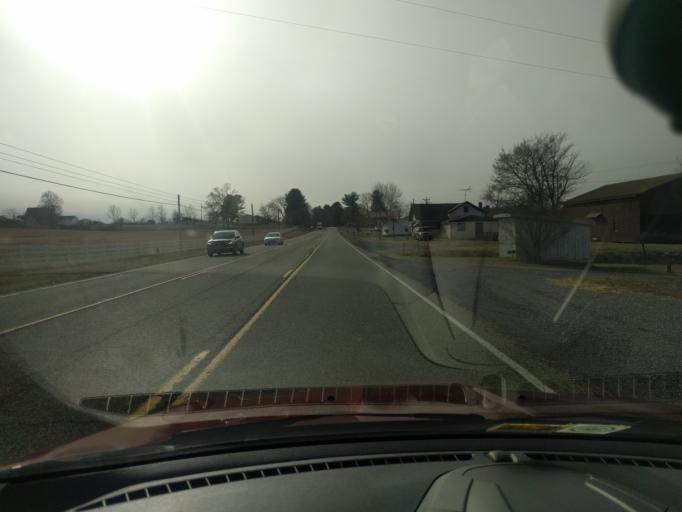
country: US
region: Virginia
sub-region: Augusta County
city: Stuarts Draft
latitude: 37.9766
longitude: -79.1713
